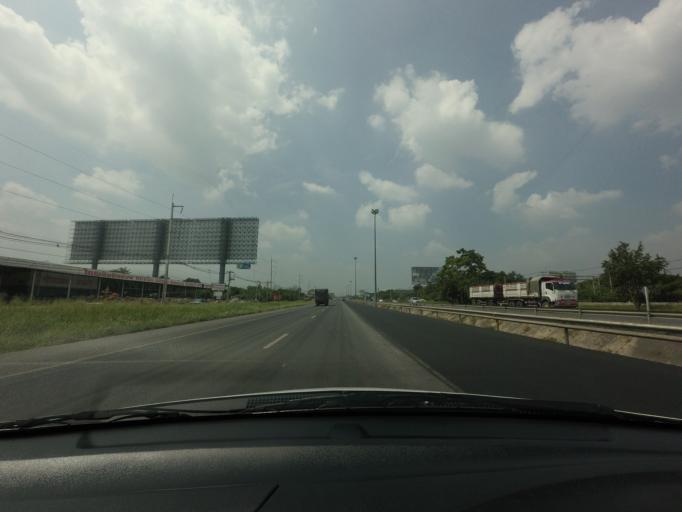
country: TH
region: Nakhon Ratchasima
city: Pak Chong
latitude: 14.6617
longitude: 101.4012
